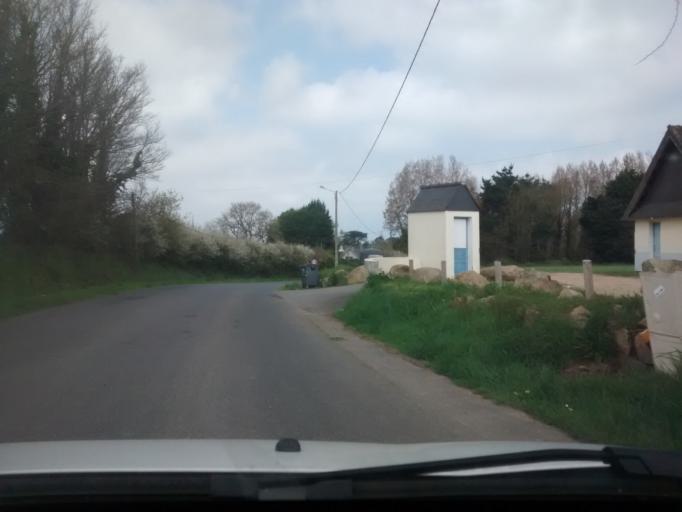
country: FR
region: Brittany
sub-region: Departement des Cotes-d'Armor
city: Trevou-Treguignec
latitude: 48.8098
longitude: -3.3549
